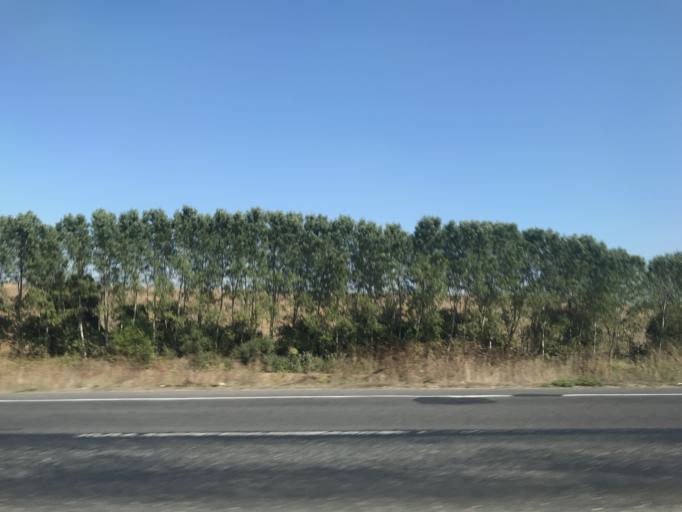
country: TR
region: Tekirdag
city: Muratli
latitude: 41.1189
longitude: 27.4885
